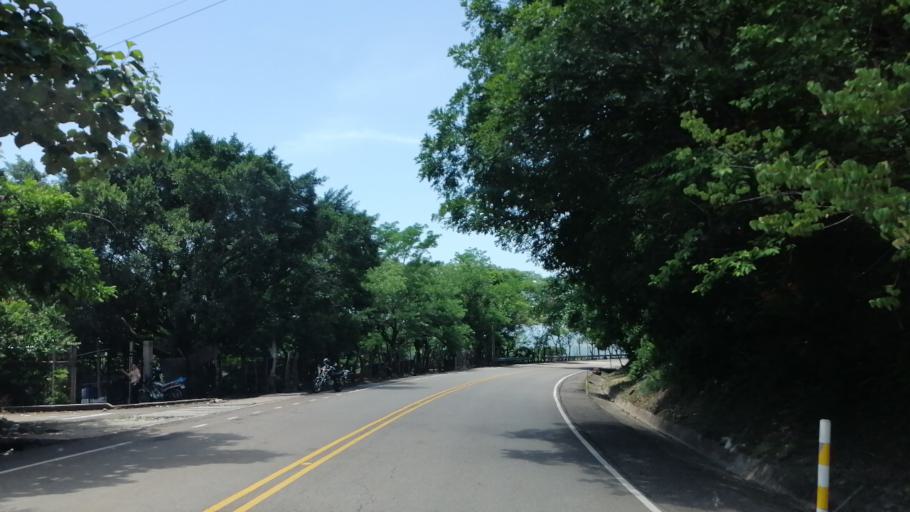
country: SV
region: Chalatenango
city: Nueva Concepcion
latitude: 14.1681
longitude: -89.3104
